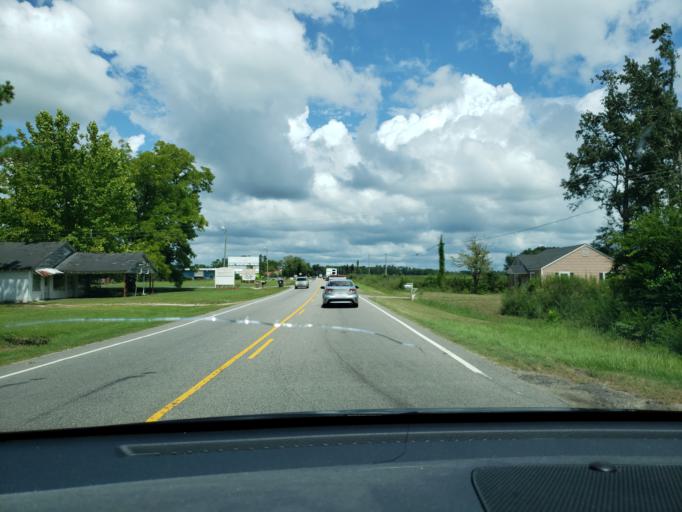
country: US
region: North Carolina
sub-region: Columbus County
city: Brunswick
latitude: 34.2714
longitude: -78.7420
